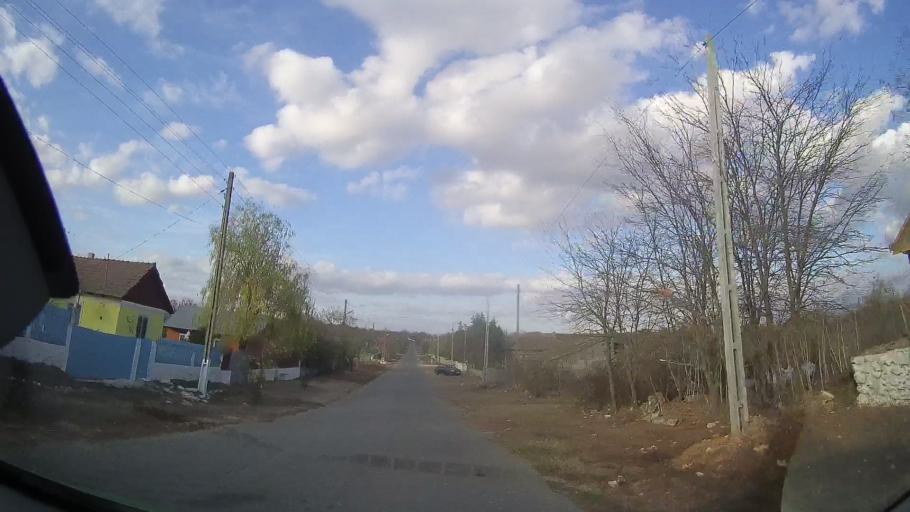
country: RO
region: Constanta
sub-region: Comuna Cerchezu
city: Cerchezu
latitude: 43.8556
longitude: 28.1012
